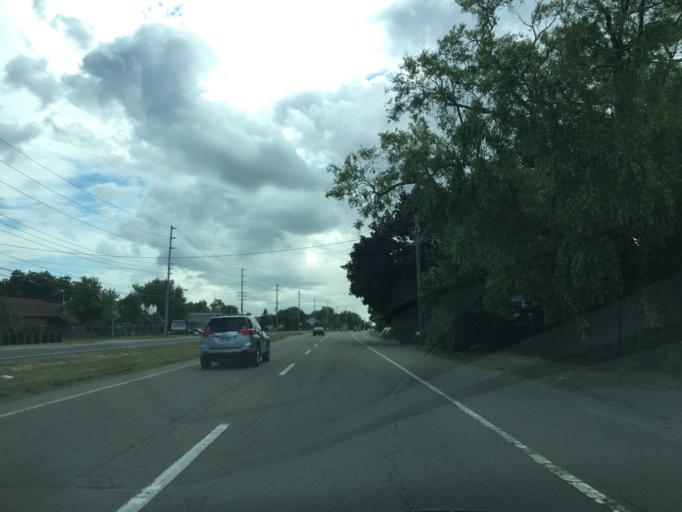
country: US
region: New York
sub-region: Suffolk County
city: Southold
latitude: 41.0534
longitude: -72.4553
